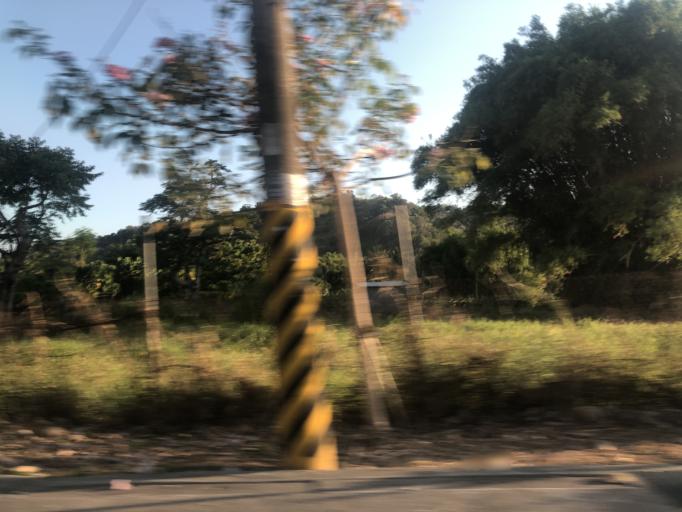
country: TW
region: Taiwan
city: Fengyuan
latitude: 24.2782
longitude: 120.7706
